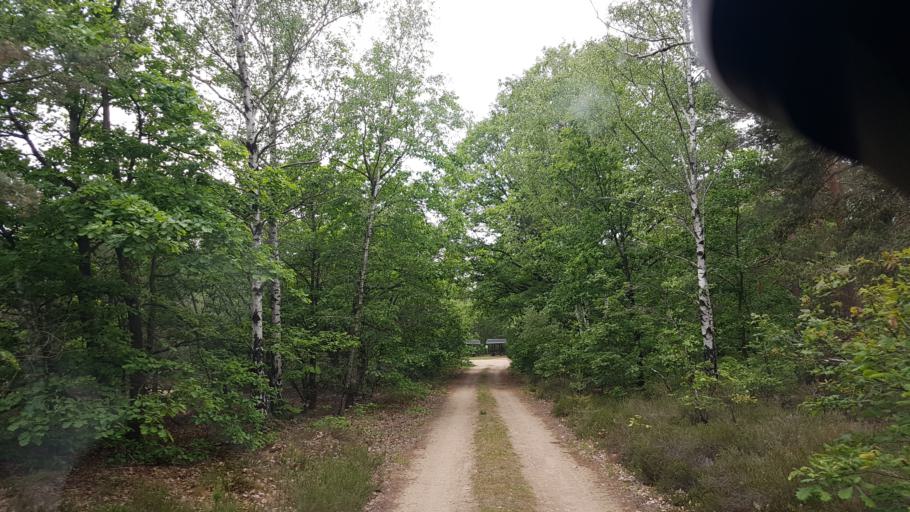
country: DE
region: Brandenburg
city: Hohenleipisch
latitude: 51.5169
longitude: 13.5101
